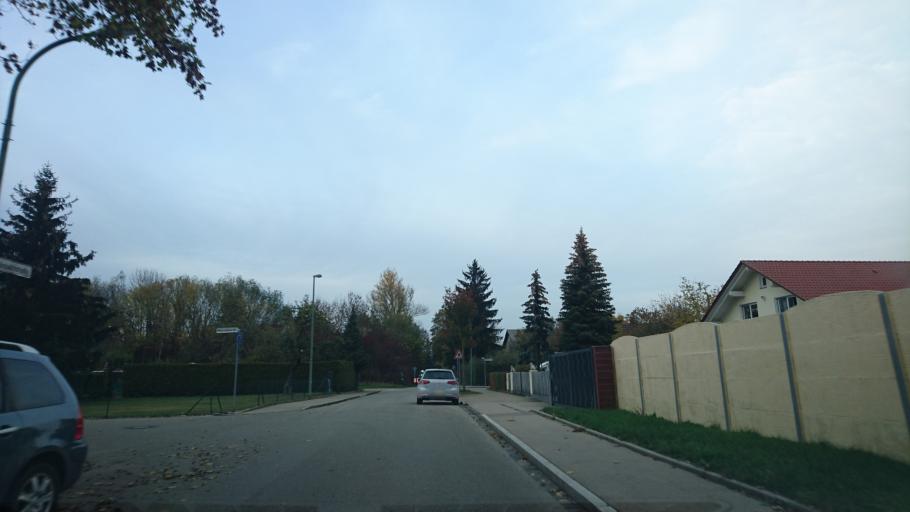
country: DE
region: Bavaria
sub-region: Swabia
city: Gersthofen
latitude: 48.4026
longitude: 10.8845
